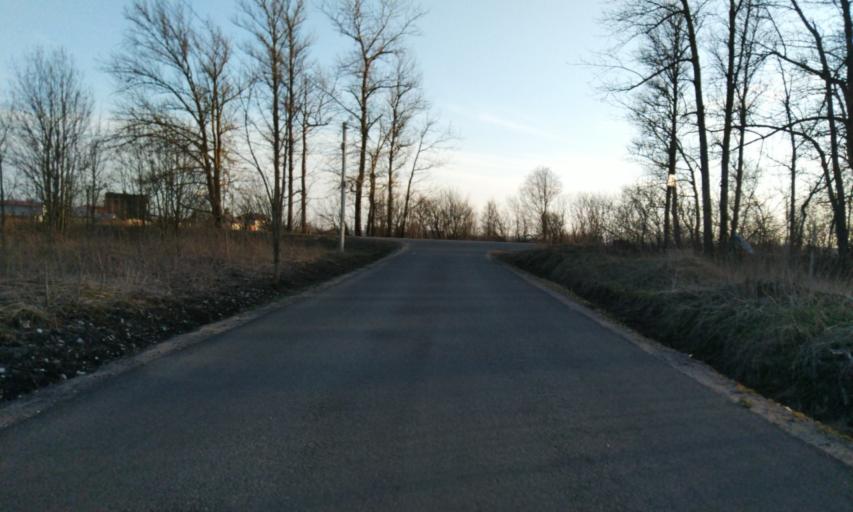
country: RU
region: Leningrad
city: Novoye Devyatkino
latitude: 60.1022
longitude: 30.4473
